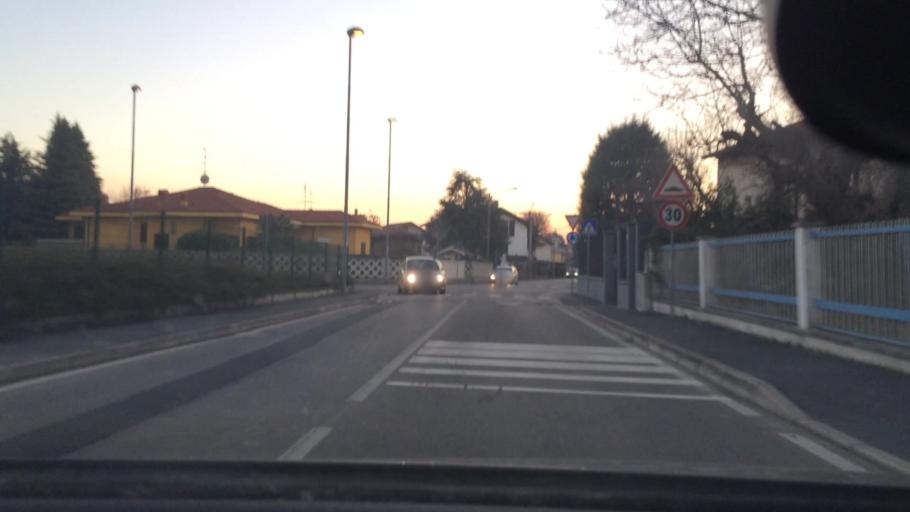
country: IT
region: Lombardy
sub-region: Provincia di Como
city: Turate
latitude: 45.6509
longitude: 9.0041
